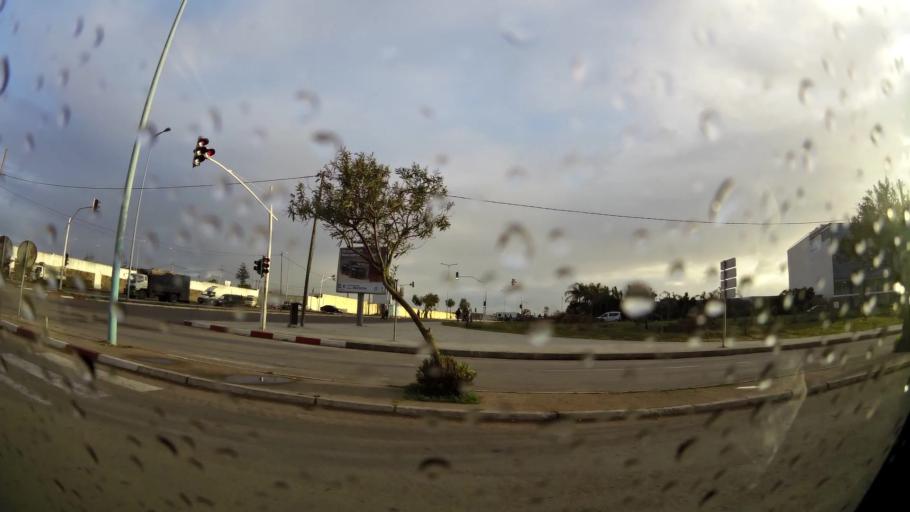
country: MA
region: Doukkala-Abda
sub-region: El-Jadida
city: El Jadida
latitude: 33.2373
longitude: -8.4829
